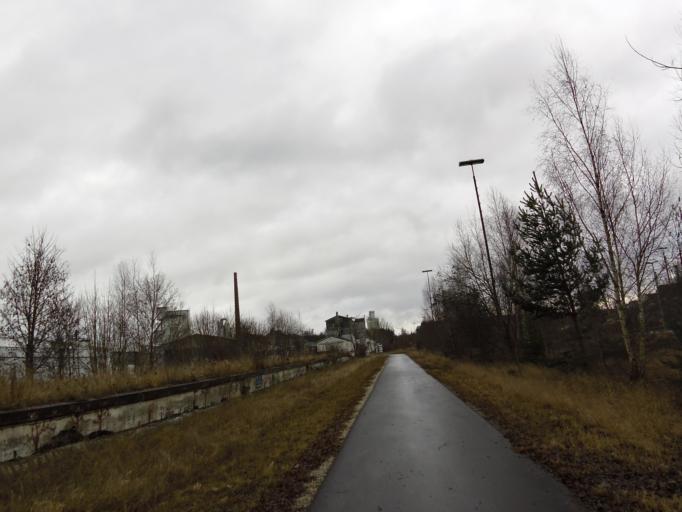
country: DE
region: Bavaria
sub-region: Upper Franconia
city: Wunsiedel
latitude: 50.0512
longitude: 12.0343
